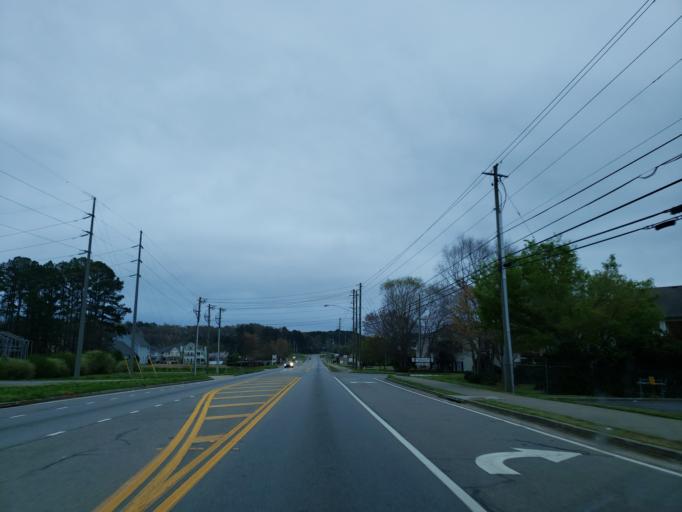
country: US
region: Georgia
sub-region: Bartow County
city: Cartersville
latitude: 34.1513
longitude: -84.8173
